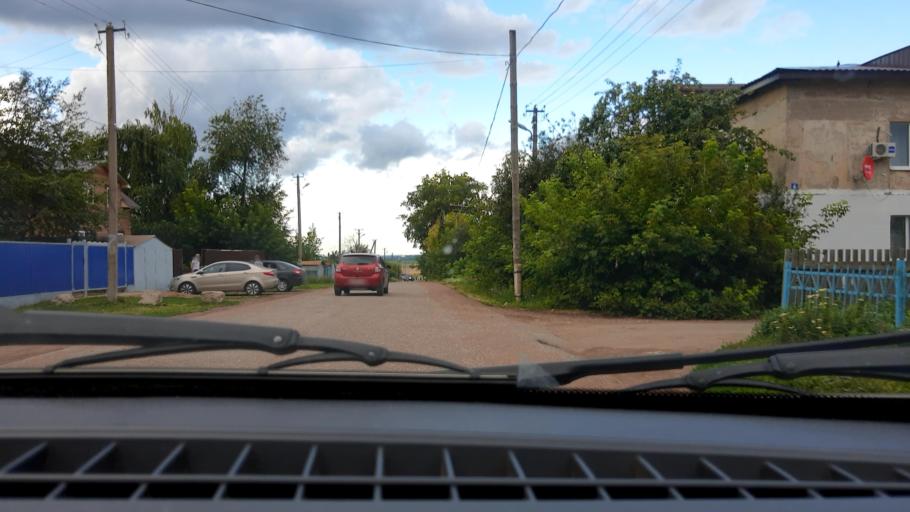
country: RU
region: Bashkortostan
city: Mikhaylovka
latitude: 54.8631
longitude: 55.8157
